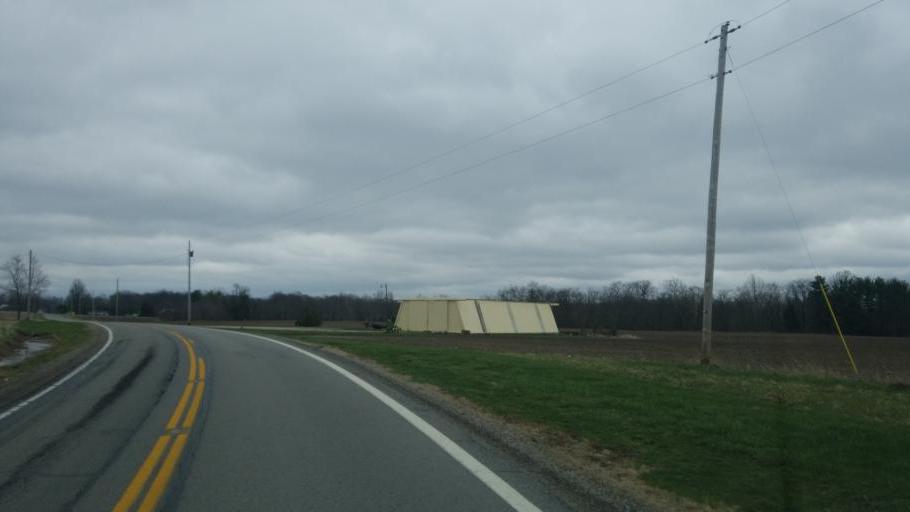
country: US
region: Ohio
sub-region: Hardin County
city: Forest
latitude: 40.6825
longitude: -83.3867
